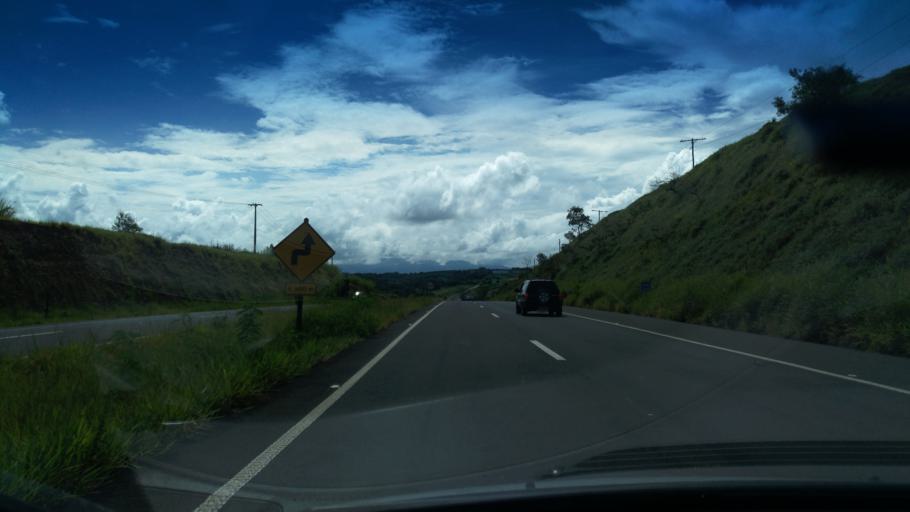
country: BR
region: Sao Paulo
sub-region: Santo Antonio Do Jardim
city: Espirito Santo do Pinhal
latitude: -22.1703
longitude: -46.7428
